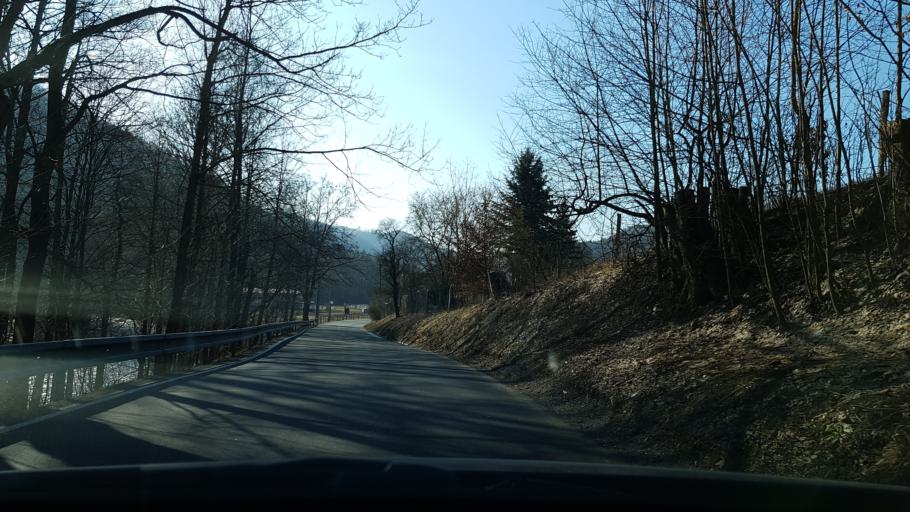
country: CZ
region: Olomoucky
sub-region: Okres Sumperk
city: Hanusovice
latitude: 50.0553
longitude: 16.9176
